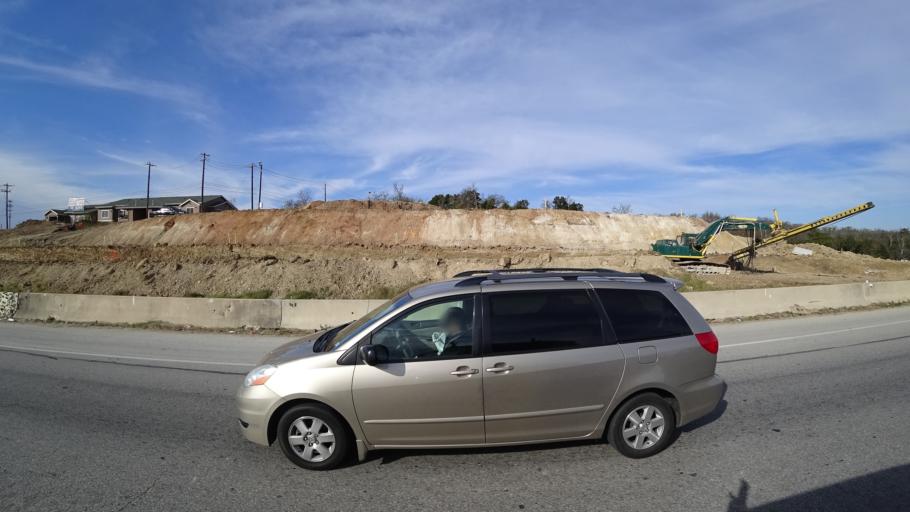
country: US
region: Texas
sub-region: Travis County
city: Austin
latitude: 30.2808
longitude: -97.6668
